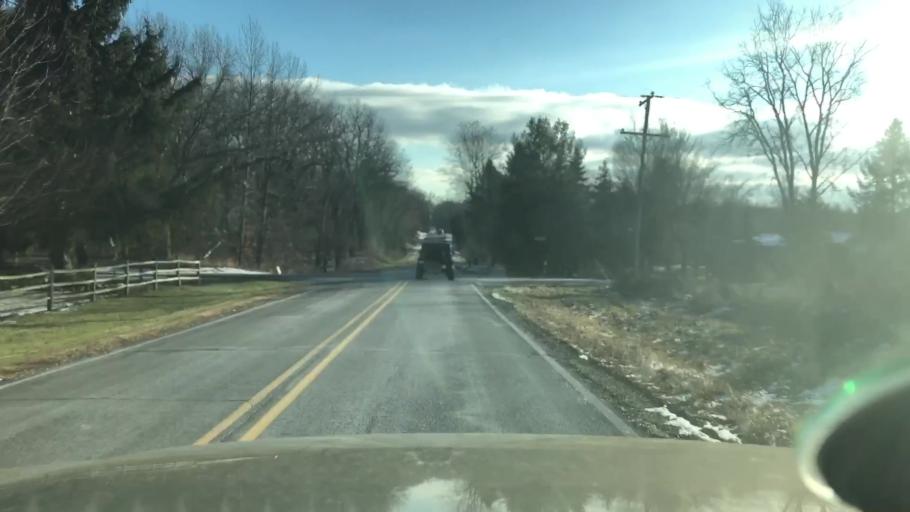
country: US
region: Michigan
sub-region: Jackson County
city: Vandercook Lake
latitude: 42.1170
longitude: -84.4514
